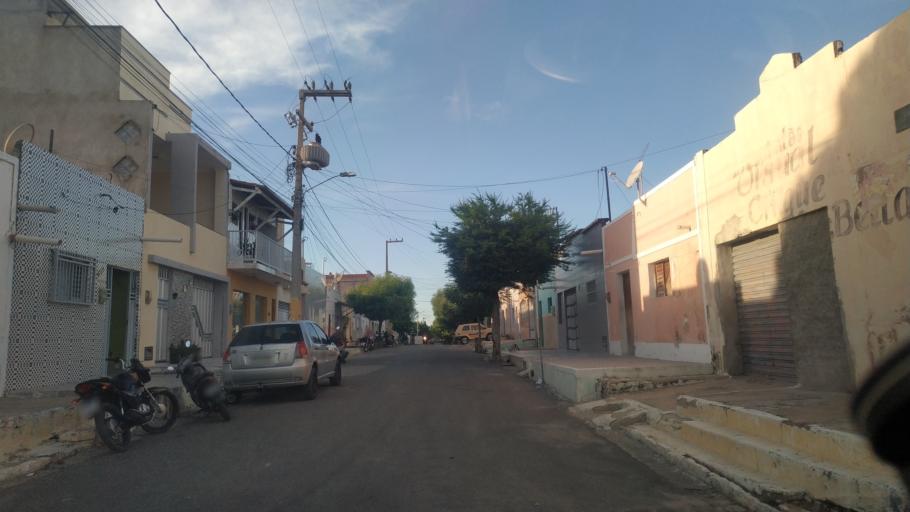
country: BR
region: Rio Grande do Norte
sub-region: Areia Branca
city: Areia Branca
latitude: -4.9519
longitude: -37.1330
